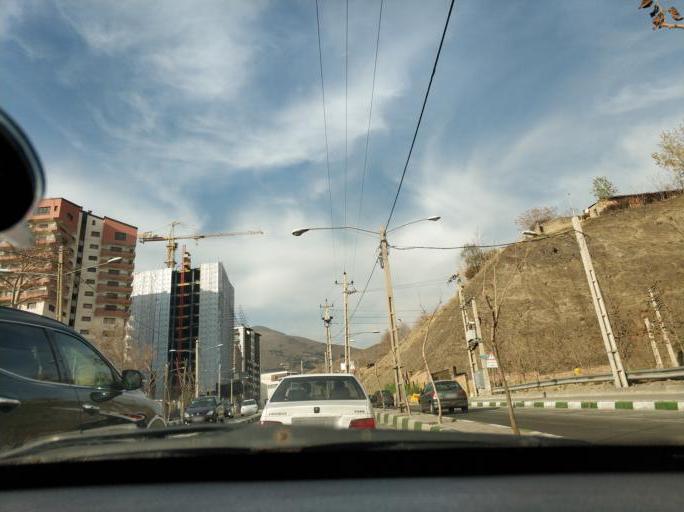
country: IR
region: Tehran
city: Tajrish
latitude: 35.8125
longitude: 51.4850
